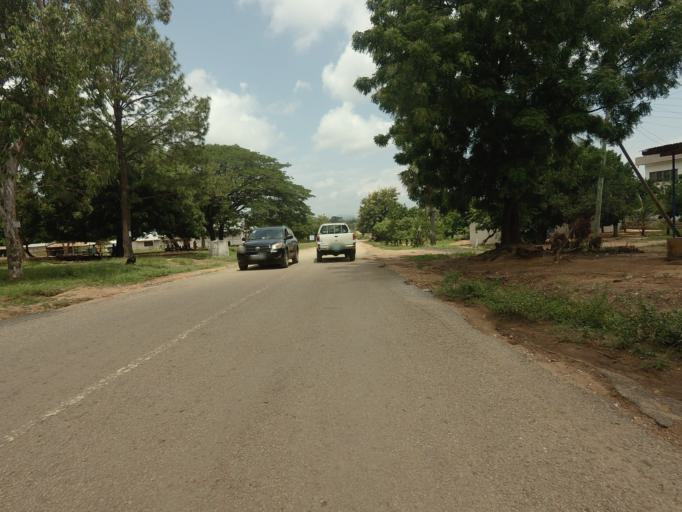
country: GH
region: Volta
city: Ho
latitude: 6.7270
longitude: 0.3444
